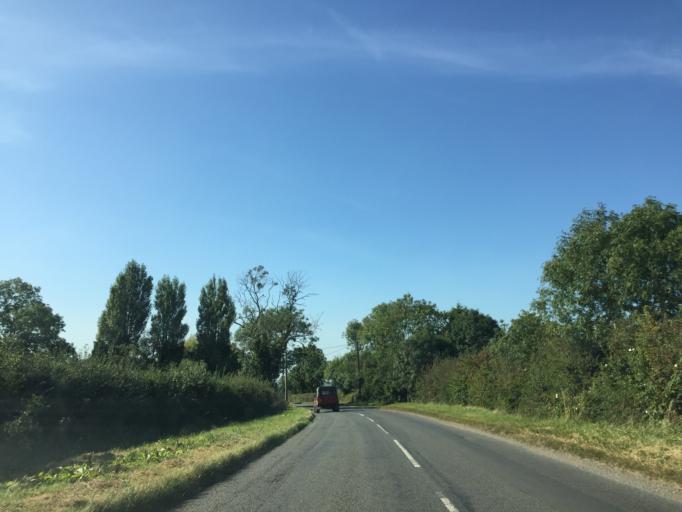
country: GB
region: England
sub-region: Leicestershire
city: Queniborough
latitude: 52.6983
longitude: -1.0054
